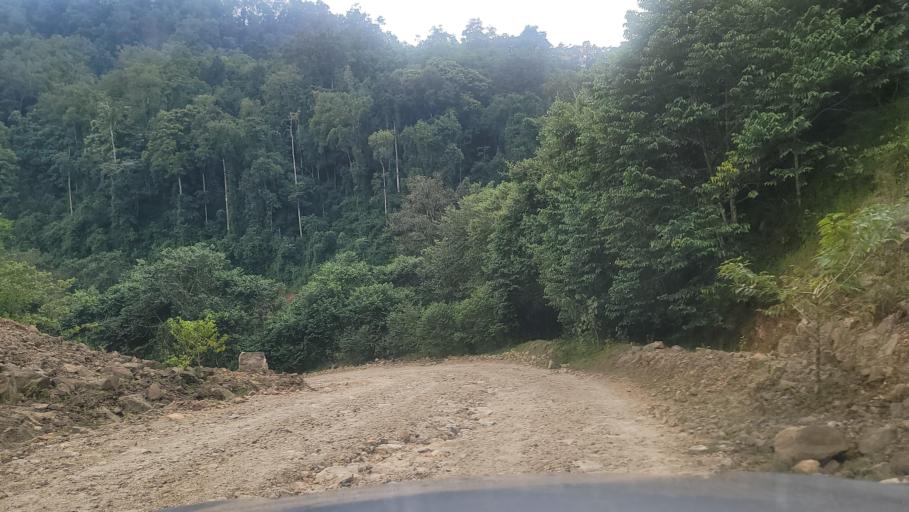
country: ET
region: Southern Nations, Nationalities, and People's Region
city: Bonga
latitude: 7.6074
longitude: 36.1987
